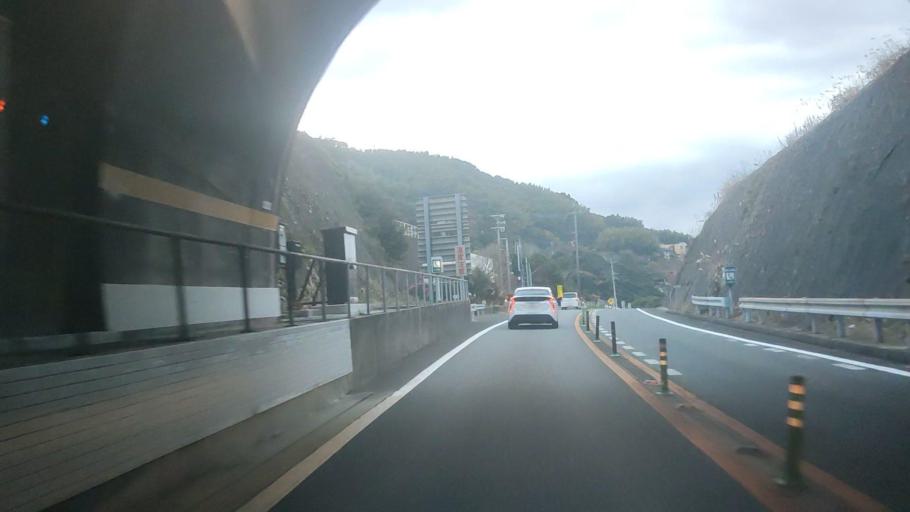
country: JP
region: Nagasaki
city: Nagasaki-shi
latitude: 32.7715
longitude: 129.8907
